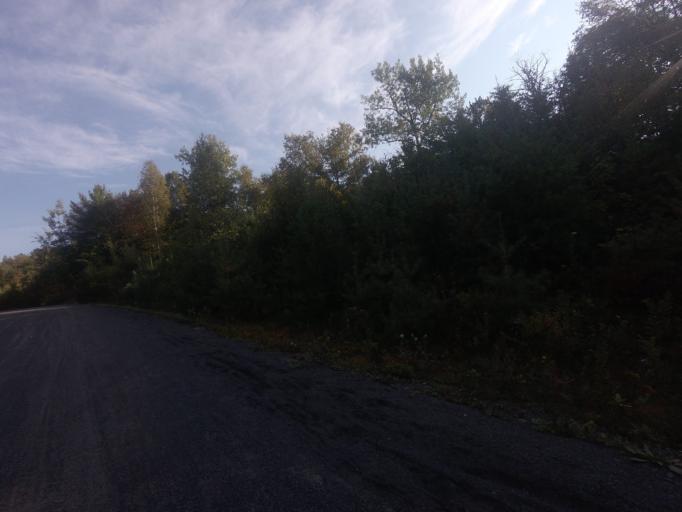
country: CA
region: Quebec
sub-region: Laurentides
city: Sainte-Adele
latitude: 45.9903
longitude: -74.1177
